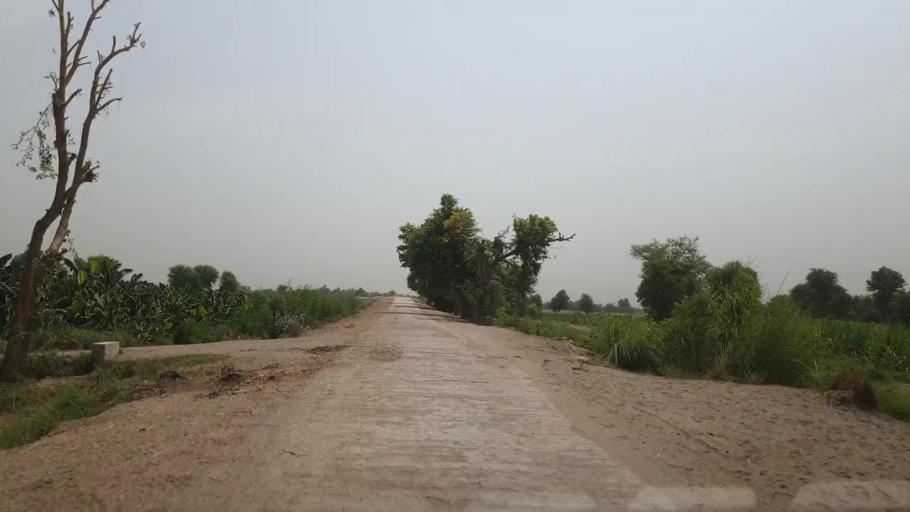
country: PK
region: Sindh
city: Gambat
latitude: 27.4433
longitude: 68.5068
